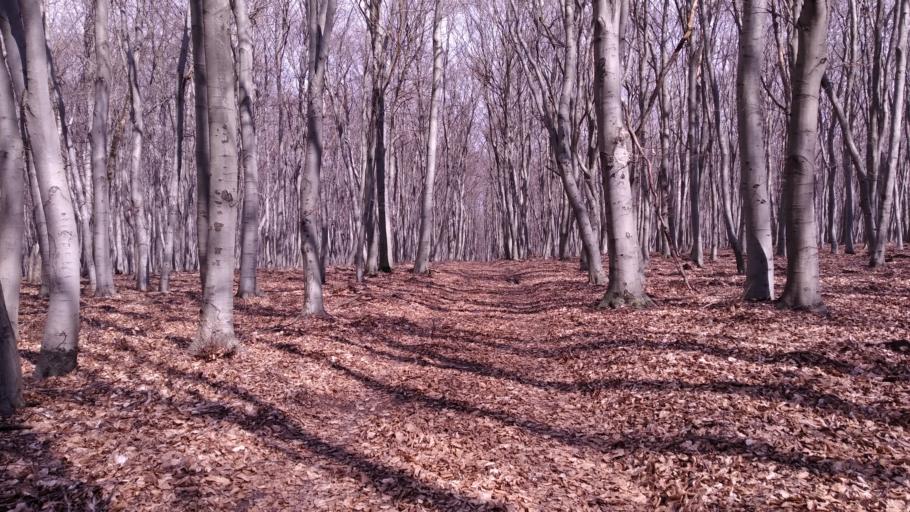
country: HU
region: Komarom-Esztergom
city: Oroszlany
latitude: 47.3991
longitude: 18.3262
